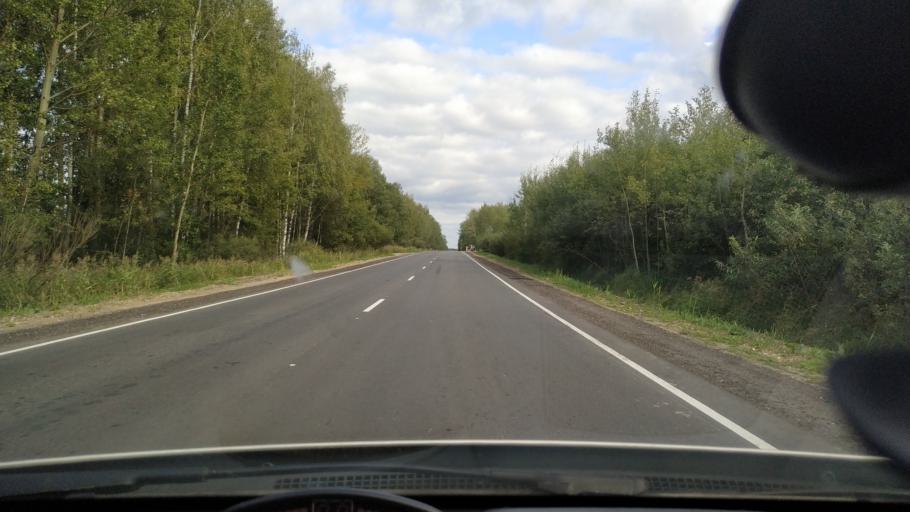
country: RU
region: Moskovskaya
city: Likino-Dulevo
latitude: 55.7276
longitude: 39.0288
